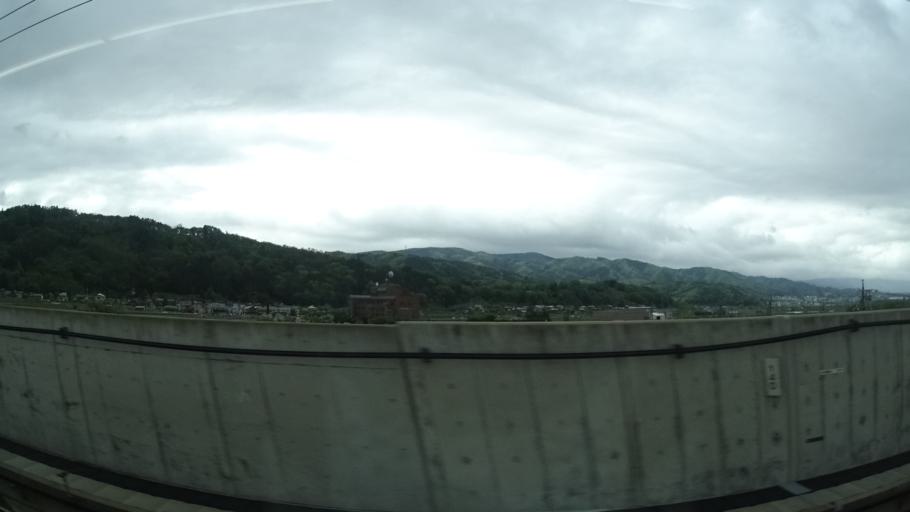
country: JP
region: Nagano
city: Nakano
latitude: 36.7882
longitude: 138.3584
